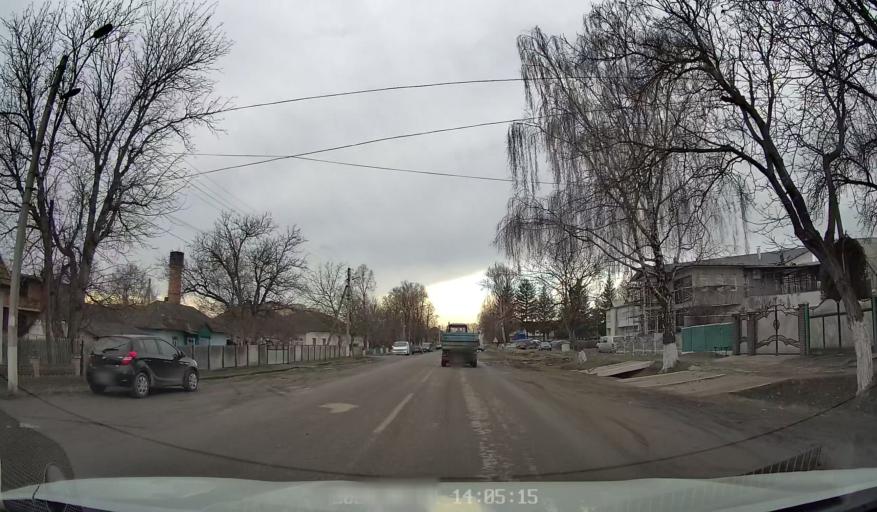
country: RO
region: Botosani
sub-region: Comuna Darabani
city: Bajura
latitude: 48.2555
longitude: 26.5781
